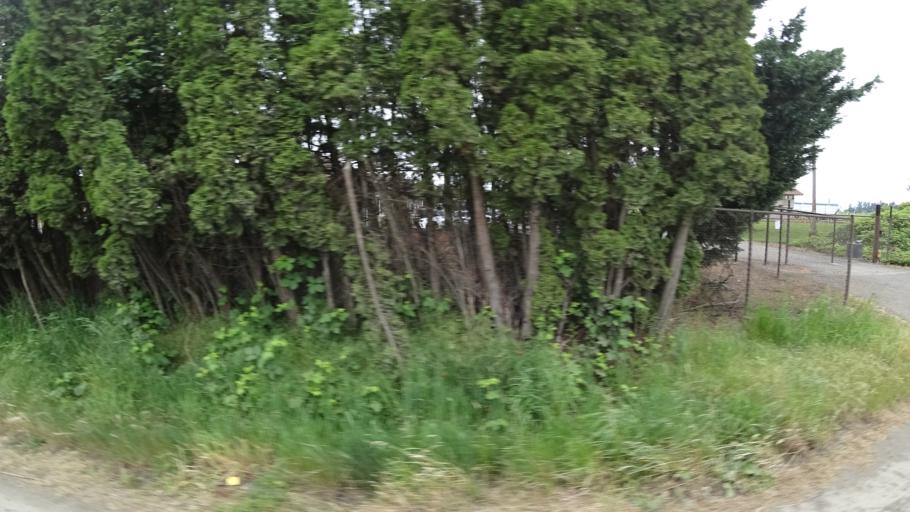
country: US
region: Oregon
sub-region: Washington County
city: Hillsboro
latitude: 45.4931
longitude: -122.9697
